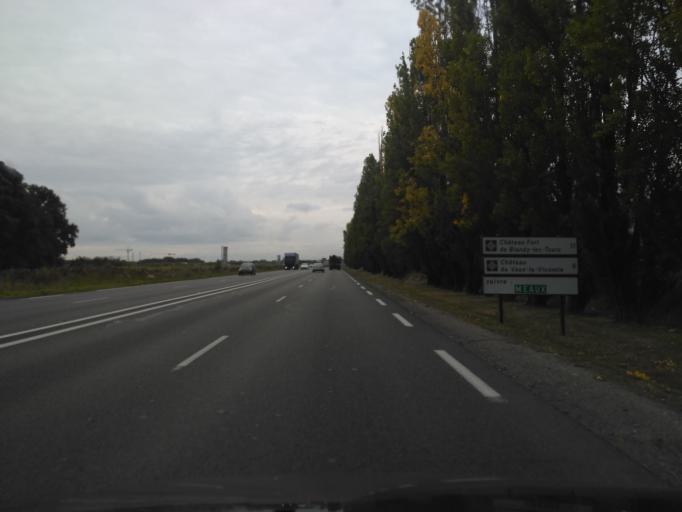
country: FR
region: Ile-de-France
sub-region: Departement de Seine-et-Marne
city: Voisenon
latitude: 48.5530
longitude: 2.6538
